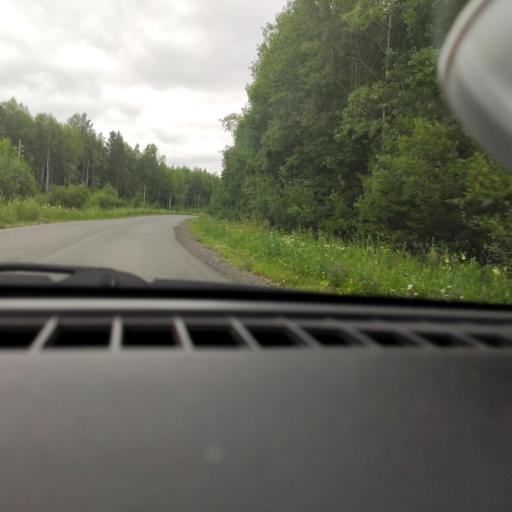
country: RU
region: Perm
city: Polazna
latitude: 58.3310
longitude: 56.1518
